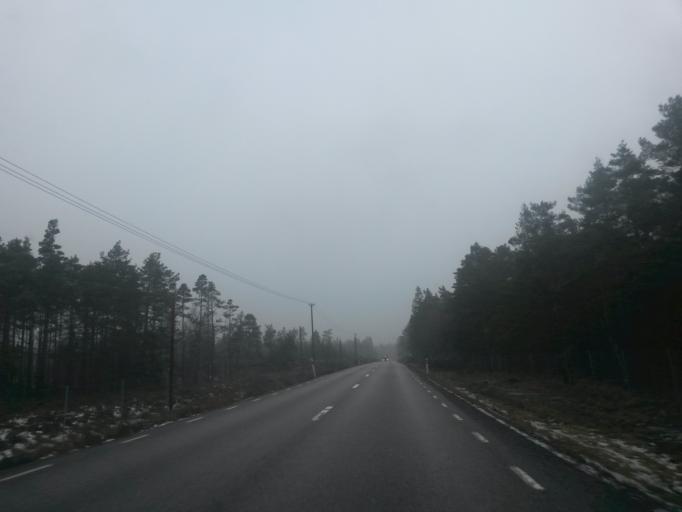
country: SE
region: Vaestra Goetaland
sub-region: Alingsas Kommun
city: Sollebrunn
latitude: 58.1949
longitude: 12.4313
